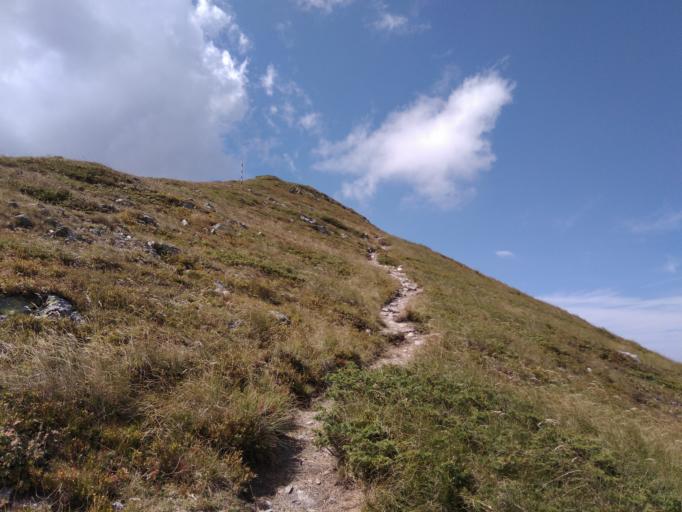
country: BG
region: Plovdiv
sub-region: Obshtina Karlovo
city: Karlovo
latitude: 42.7245
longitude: 24.7919
